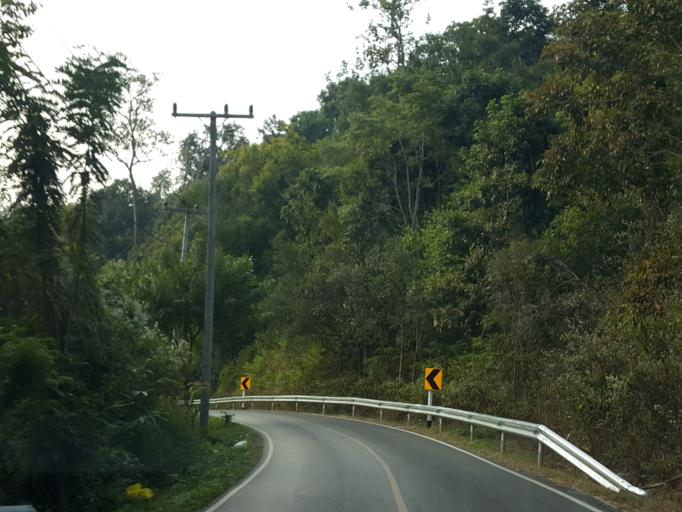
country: TH
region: Chiang Mai
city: Mae On
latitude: 18.8458
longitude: 99.2846
